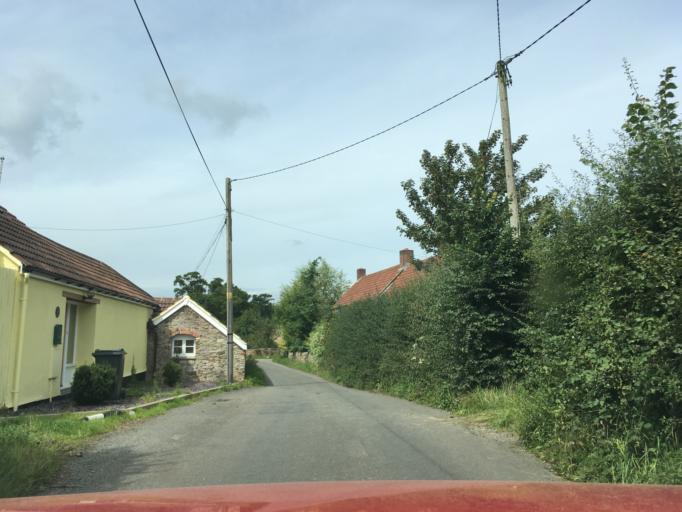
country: GB
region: England
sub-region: South Gloucestershire
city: Charfield
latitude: 51.6443
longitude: -2.4143
